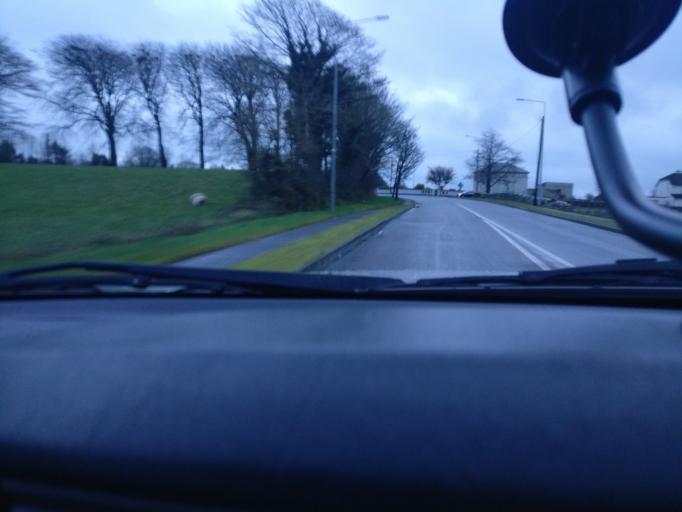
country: IE
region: Connaught
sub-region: County Galway
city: Loughrea
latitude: 53.2326
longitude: -8.4535
